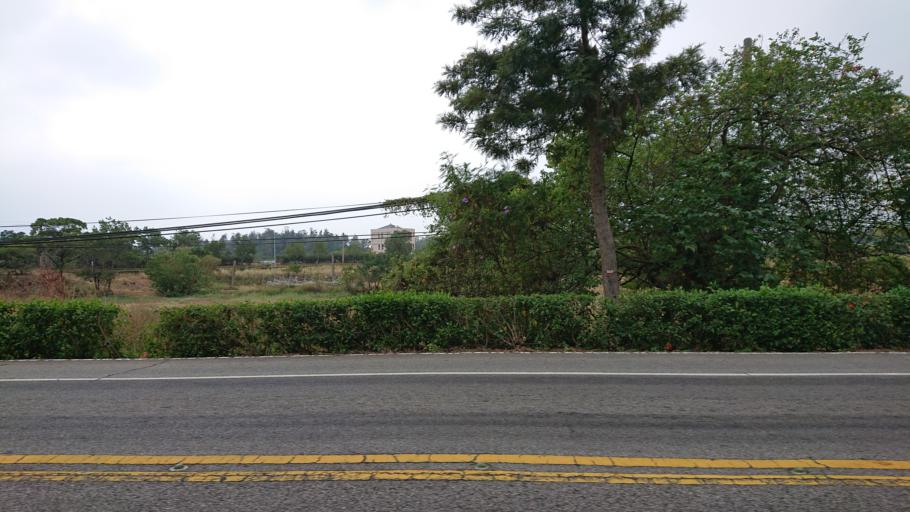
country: TW
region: Fukien
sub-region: Kinmen
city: Jincheng
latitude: 24.4443
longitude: 118.3876
